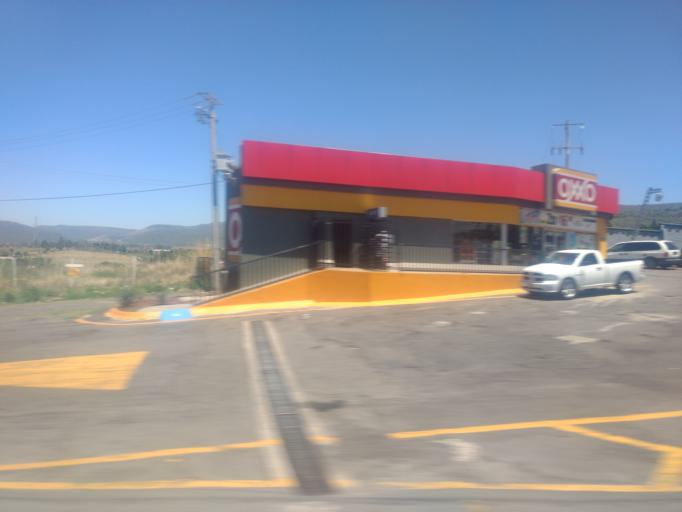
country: MX
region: Jalisco
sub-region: Acatlan de Juarez
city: Villa de los Ninos
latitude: 20.4397
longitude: -103.5253
